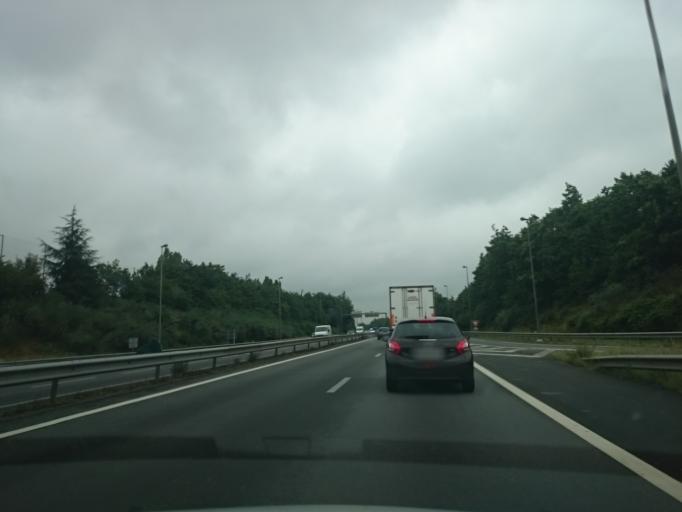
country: FR
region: Pays de la Loire
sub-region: Departement de la Loire-Atlantique
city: Saint-Herblain
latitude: 47.2185
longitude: -1.6240
